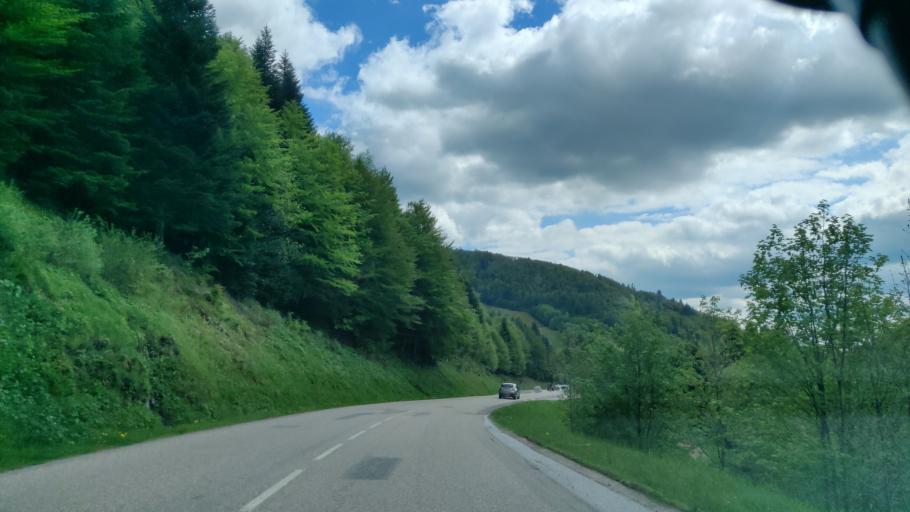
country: FR
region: Lorraine
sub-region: Departement des Vosges
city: Xonrupt-Longemer
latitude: 48.0433
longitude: 6.9761
